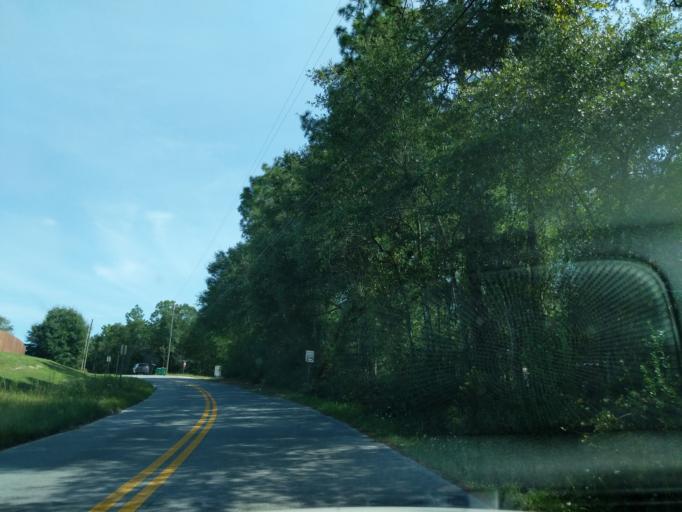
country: US
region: Florida
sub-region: Okaloosa County
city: Crestview
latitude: 30.7061
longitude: -86.5953
